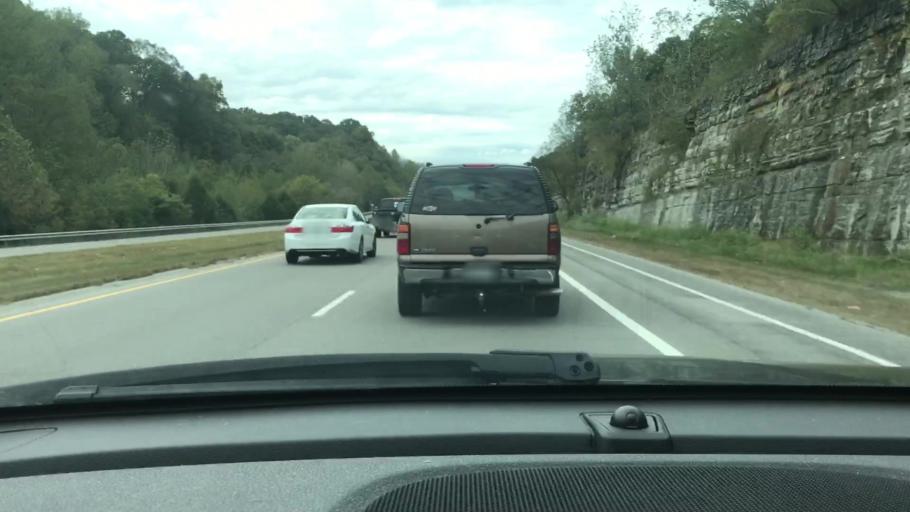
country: US
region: Tennessee
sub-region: Cheatham County
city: Ashland City
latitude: 36.2097
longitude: -86.9546
